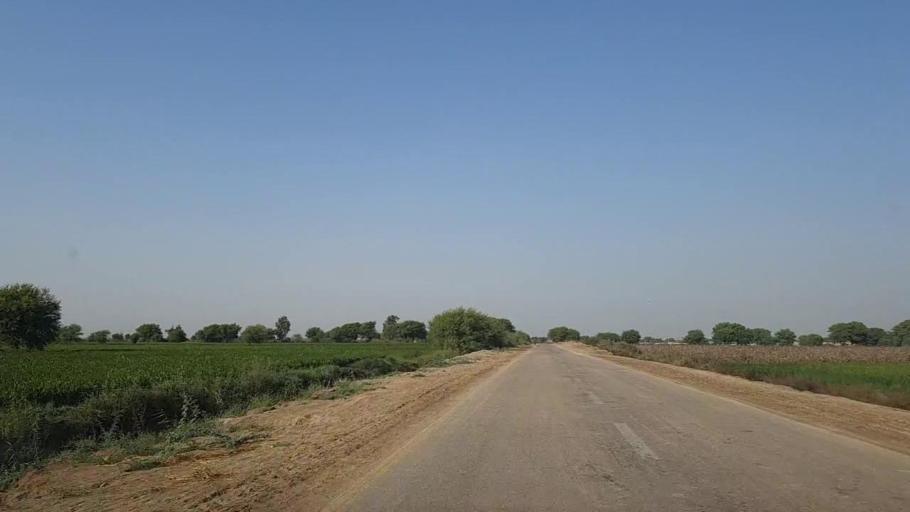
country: PK
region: Sindh
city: Mirpur Batoro
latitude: 24.5748
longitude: 68.3944
